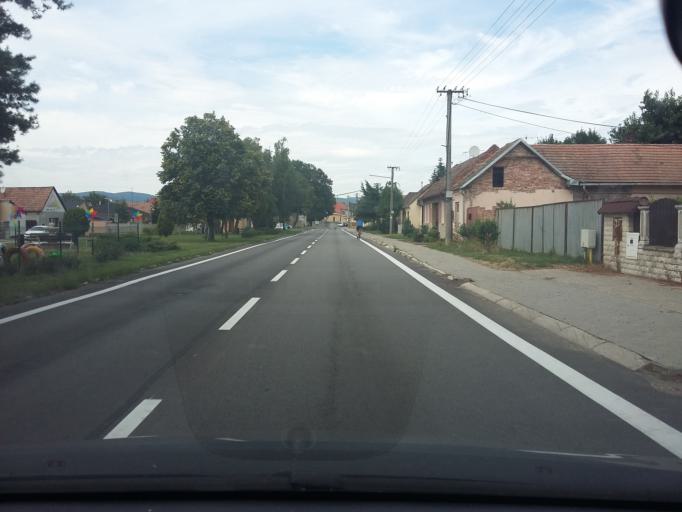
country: SK
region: Bratislavsky
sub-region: Okres Pezinok
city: Pezinok
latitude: 48.2706
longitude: 17.3028
